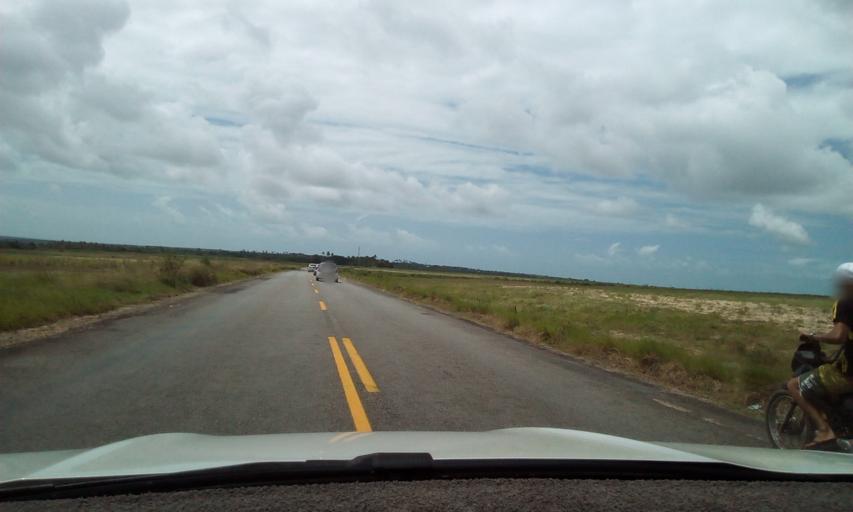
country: BR
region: Paraiba
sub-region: Rio Tinto
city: Rio Tinto
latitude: -6.7735
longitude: -35.0397
